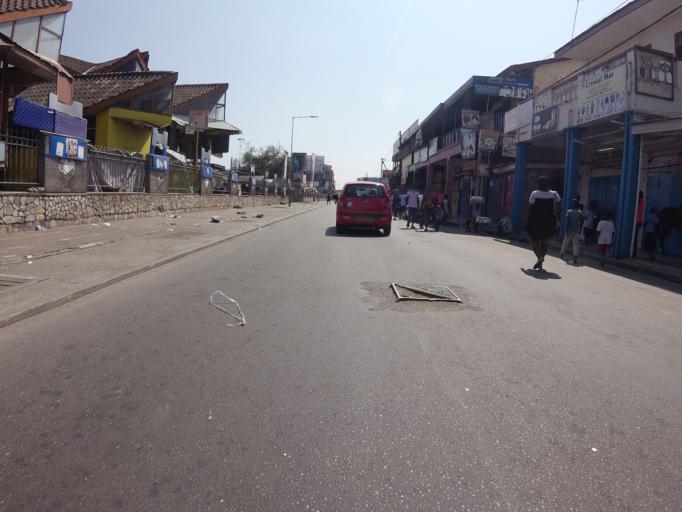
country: GH
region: Greater Accra
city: Accra
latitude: 5.5460
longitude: -0.2081
